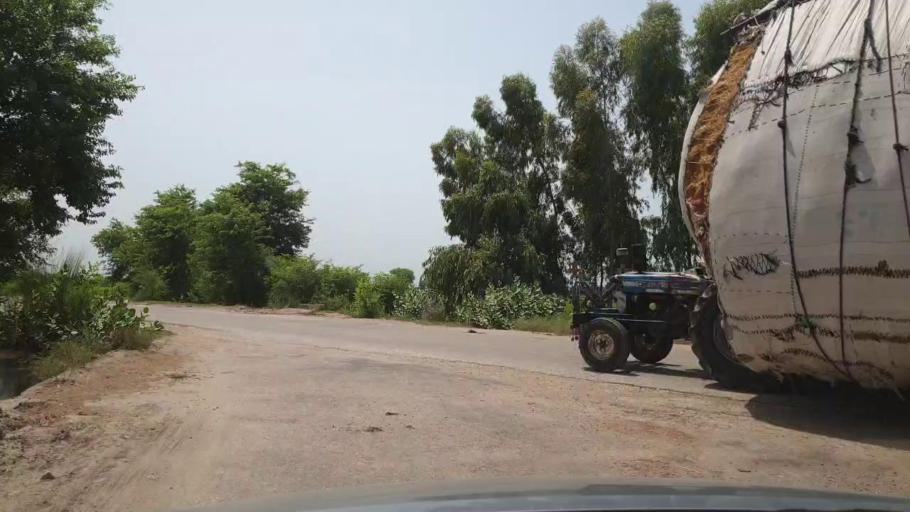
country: PK
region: Sindh
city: Madeji
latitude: 27.7726
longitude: 68.4323
